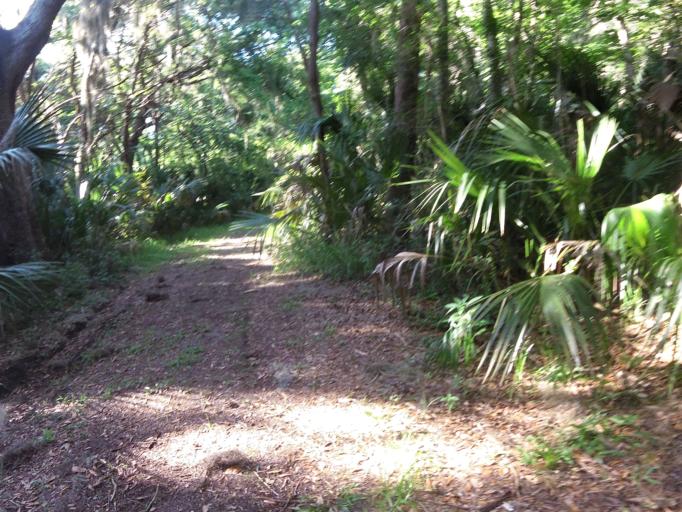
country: US
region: Florida
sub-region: Duval County
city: Atlantic Beach
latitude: 30.4390
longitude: -81.4698
